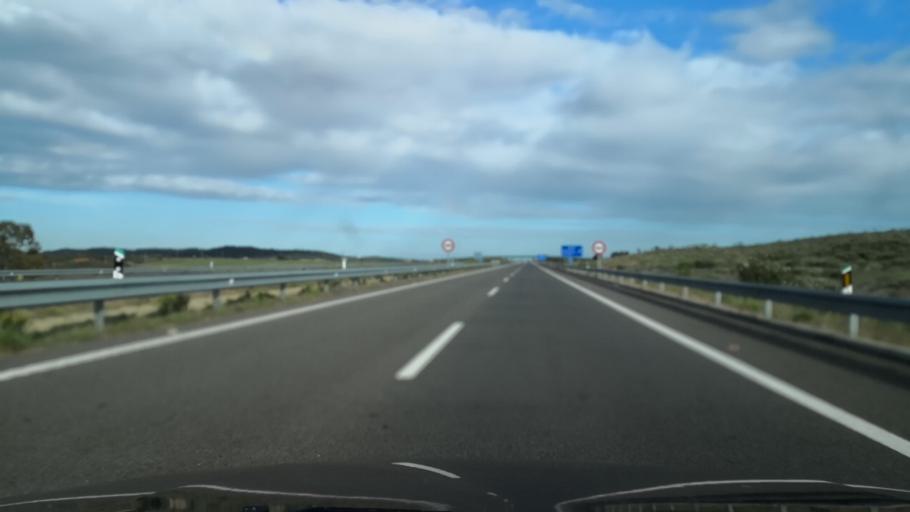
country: ES
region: Extremadura
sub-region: Provincia de Caceres
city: Casas de Don Gomez
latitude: 40.0225
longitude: -6.5983
